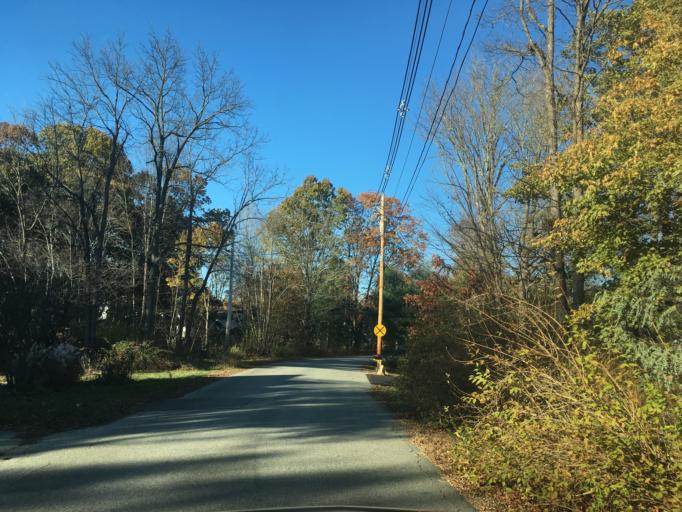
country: US
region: New Hampshire
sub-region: Rockingham County
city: Exeter
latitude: 42.9849
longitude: -70.9546
